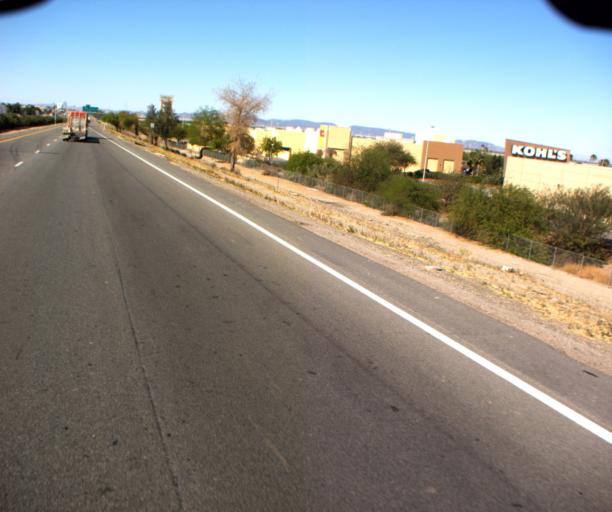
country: US
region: Arizona
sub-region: Yuma County
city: Yuma
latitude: 32.7033
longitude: -114.6098
